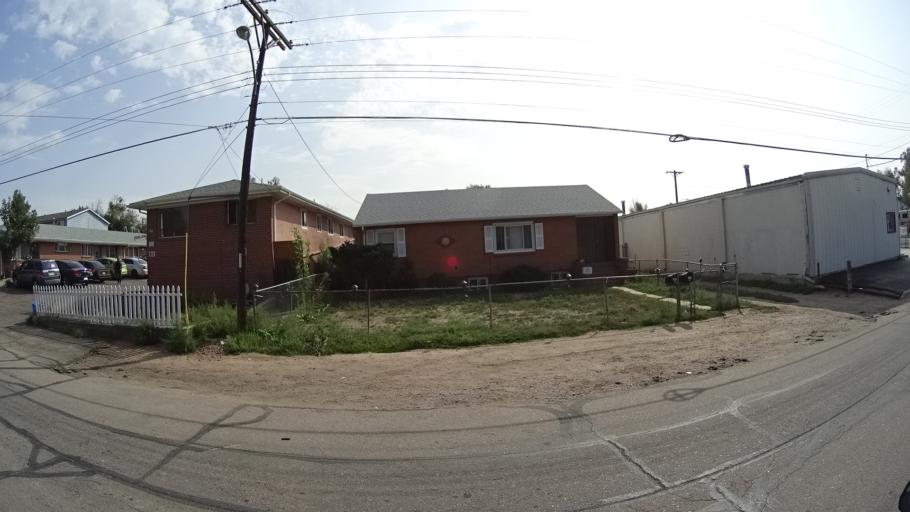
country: US
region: Colorado
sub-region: El Paso County
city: Colorado Springs
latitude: 38.8387
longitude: -104.7874
